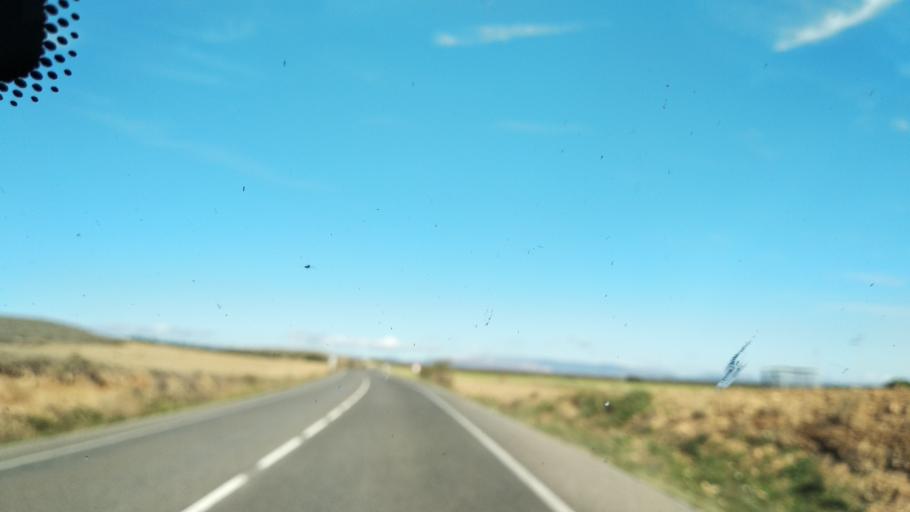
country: ES
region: Catalonia
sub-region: Provincia de Lleida
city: Termens
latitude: 41.7205
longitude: 0.7281
